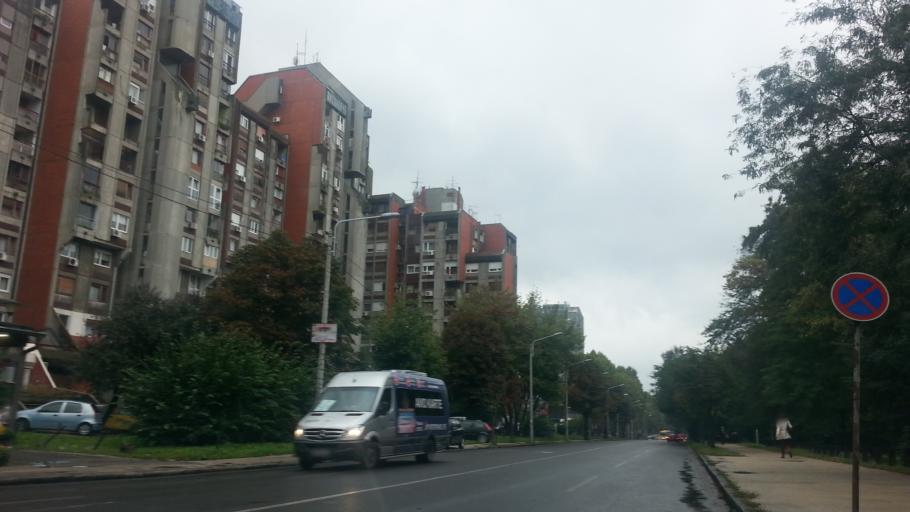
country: RS
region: Central Serbia
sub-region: Belgrade
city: Vozdovac
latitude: 44.7612
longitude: 20.4797
